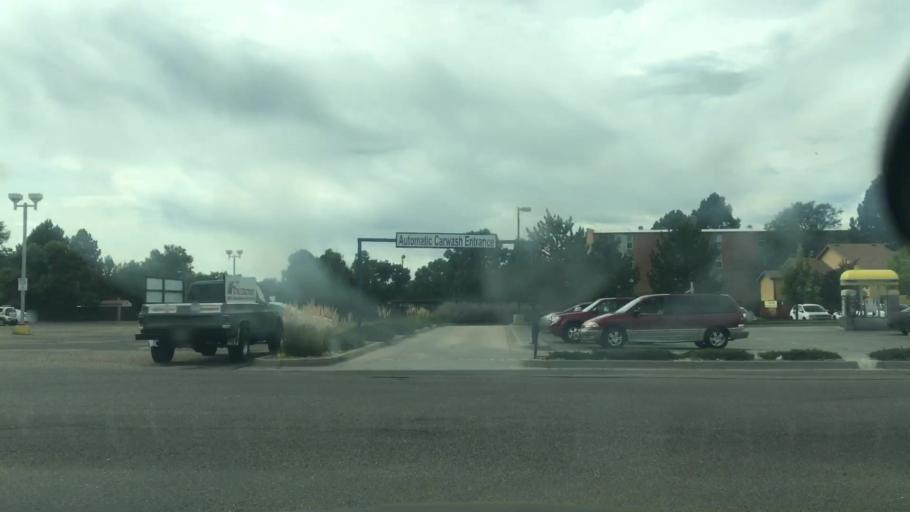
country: US
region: Colorado
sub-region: Arapahoe County
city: Glendale
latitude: 39.6768
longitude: -104.9118
